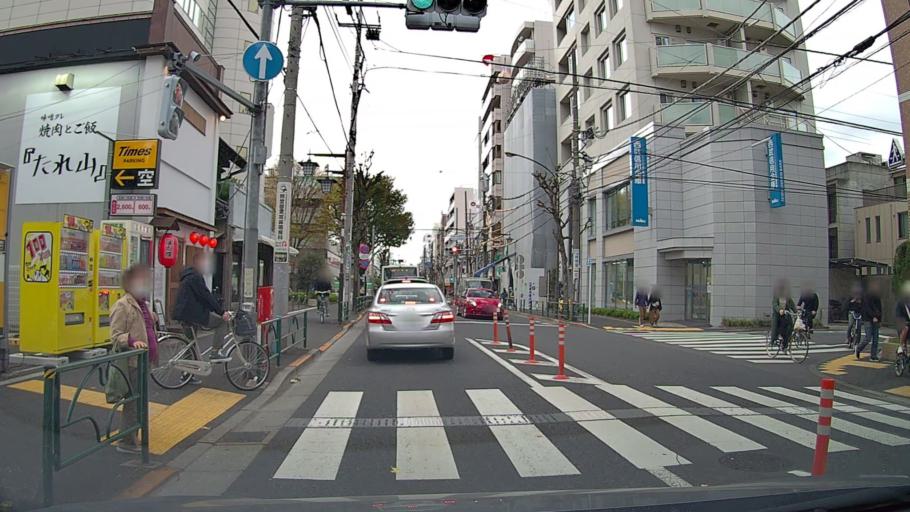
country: JP
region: Tokyo
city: Tokyo
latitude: 35.7100
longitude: 139.6644
